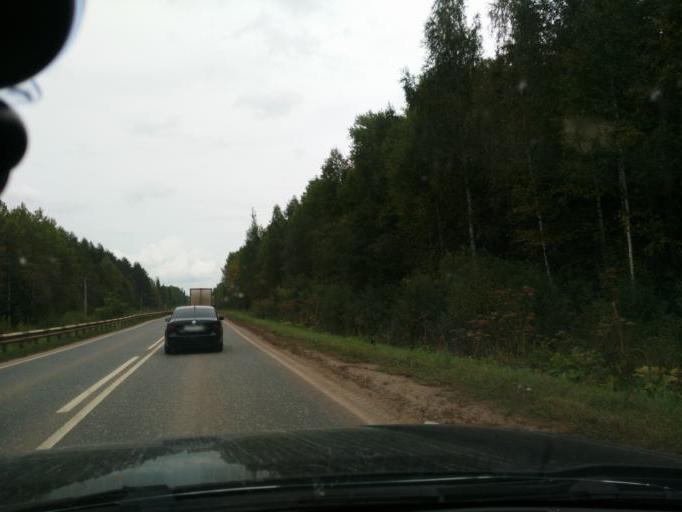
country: RU
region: Bashkortostan
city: Verkhniye Tatyshly
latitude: 56.4983
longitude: 55.8429
